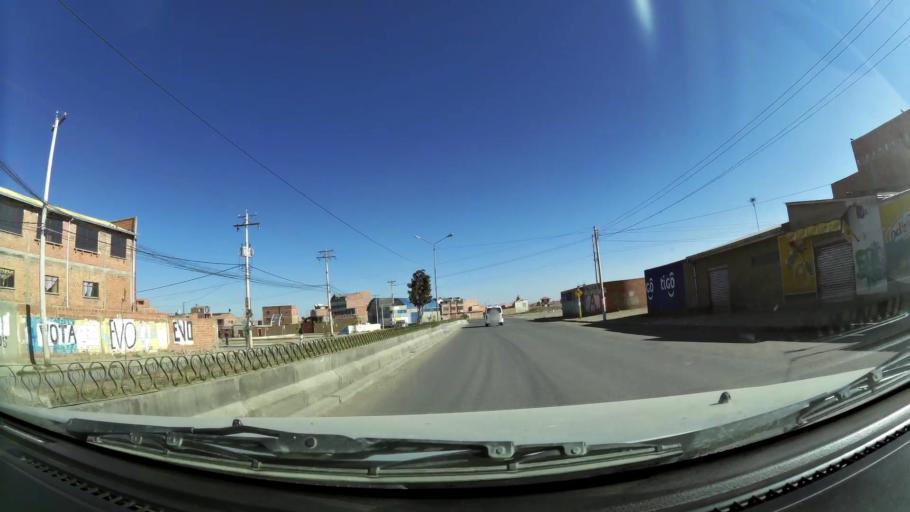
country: BO
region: La Paz
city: La Paz
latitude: -16.5158
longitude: -68.2114
